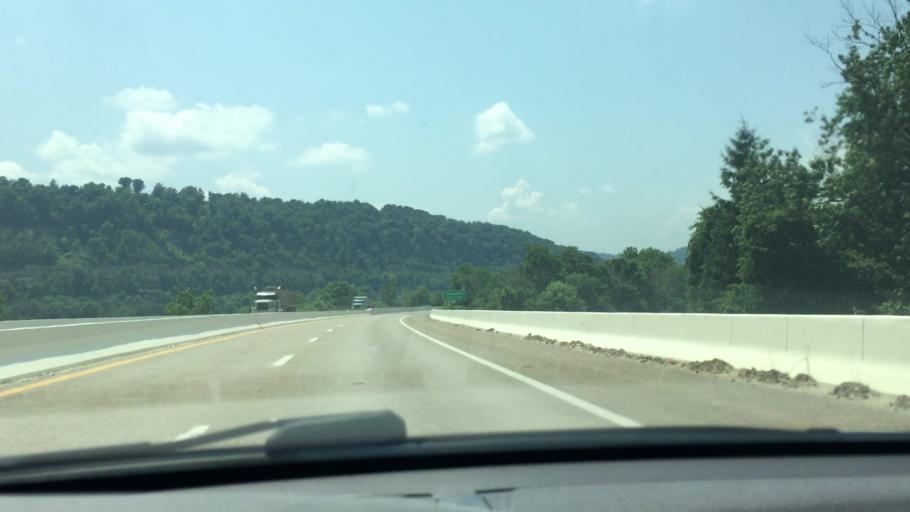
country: US
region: Ohio
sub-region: Belmont County
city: Shadyside
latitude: 39.9722
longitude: -80.7424
